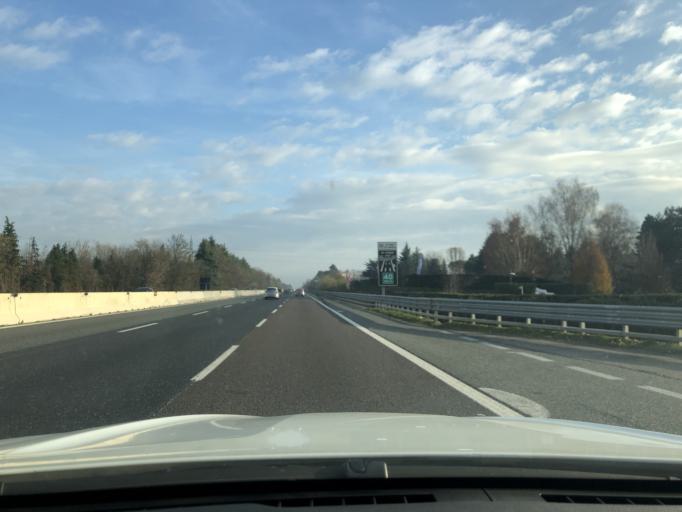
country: IT
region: Lombardy
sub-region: Provincia di Varese
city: Olgiate Olona
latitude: 45.6363
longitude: 8.8660
